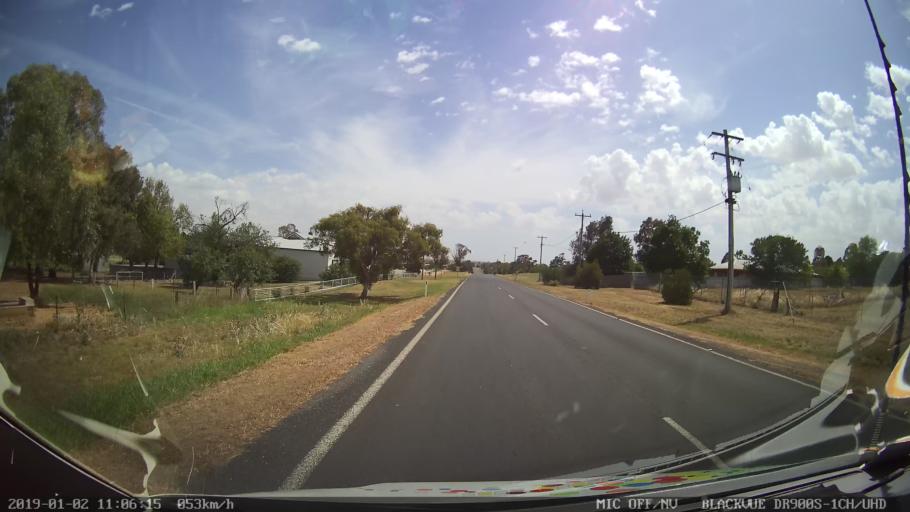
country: AU
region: New South Wales
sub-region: Young
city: Young
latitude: -34.5565
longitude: 148.3559
